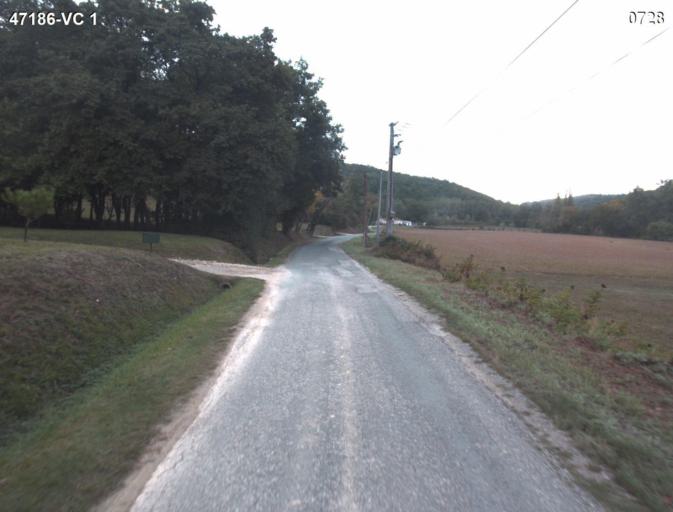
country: FR
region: Aquitaine
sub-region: Departement du Lot-et-Garonne
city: Port-Sainte-Marie
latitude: 44.1943
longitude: 0.4407
